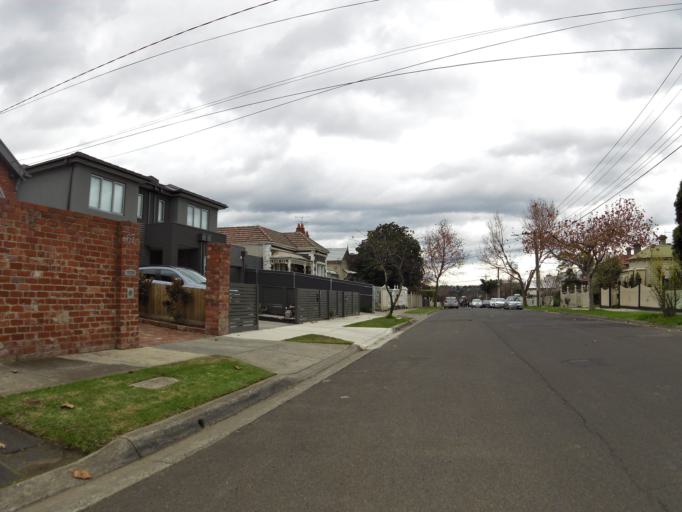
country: AU
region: Victoria
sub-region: Moonee Valley
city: Moonee Ponds
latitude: -37.7578
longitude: 144.9276
